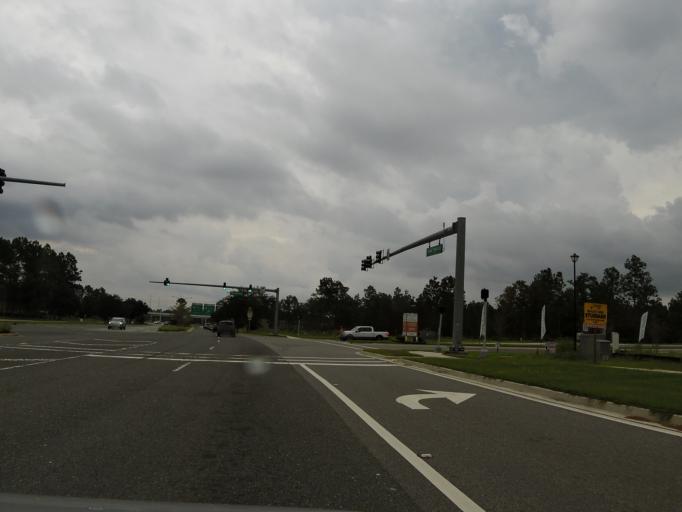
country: US
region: Florida
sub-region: Clay County
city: Lakeside
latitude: 30.1593
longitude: -81.8353
